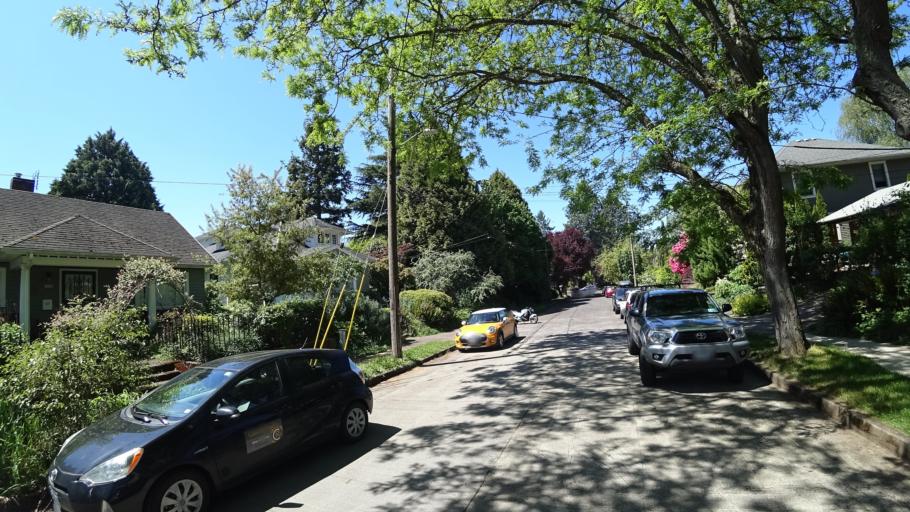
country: US
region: Oregon
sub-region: Multnomah County
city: Portland
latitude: 45.5061
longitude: -122.6285
